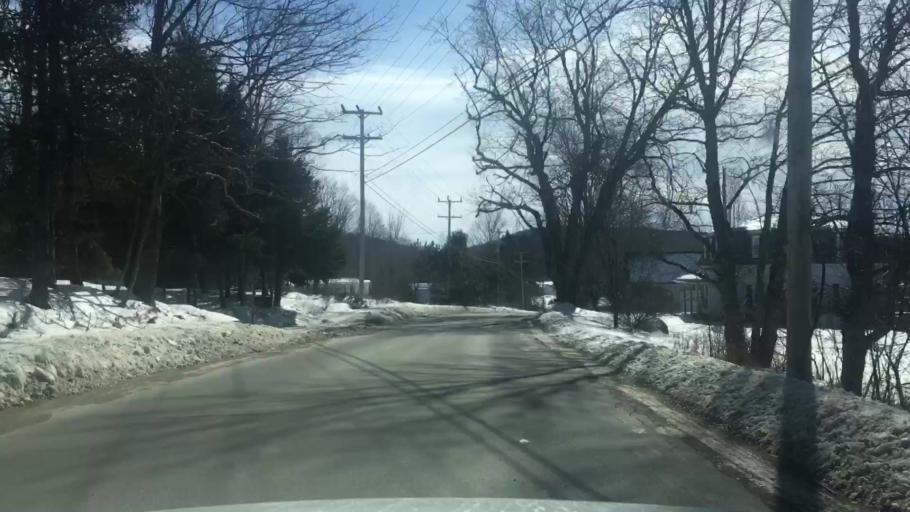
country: US
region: Maine
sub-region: Penobscot County
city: Holden
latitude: 44.7417
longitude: -68.6293
